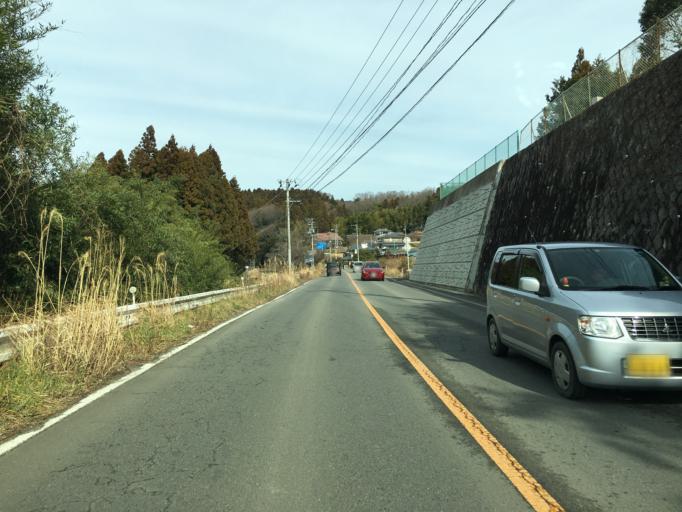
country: JP
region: Fukushima
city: Iwaki
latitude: 37.1204
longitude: 140.8715
